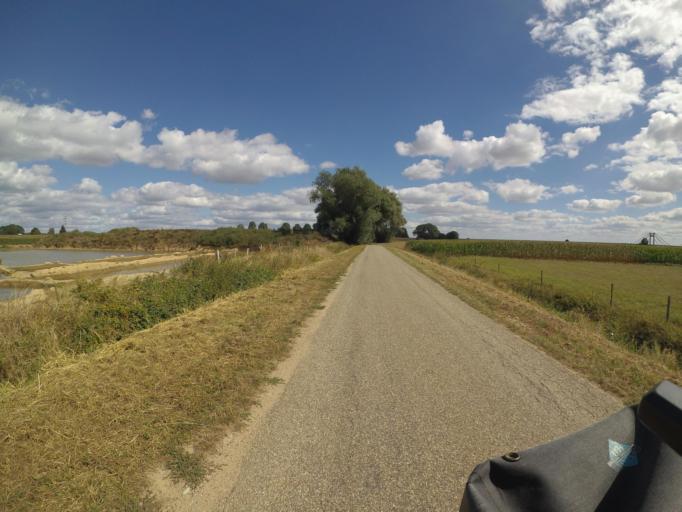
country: NL
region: Gelderland
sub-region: Gemeente Tiel
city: Tiel
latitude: 51.8989
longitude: 5.4825
